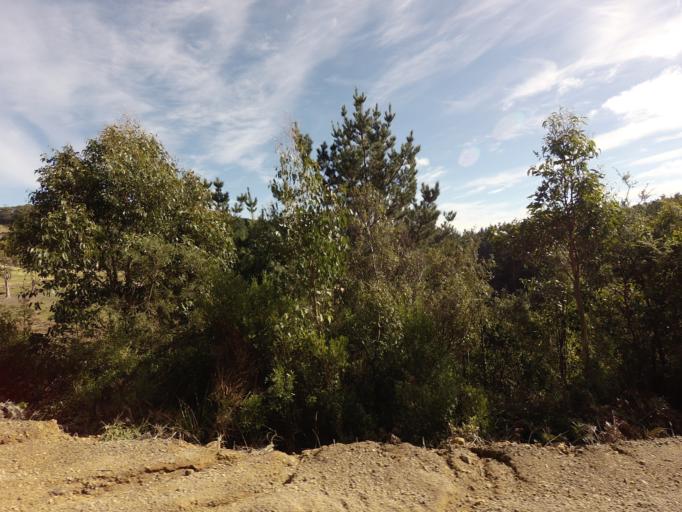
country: AU
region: Tasmania
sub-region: Clarence
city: Sandford
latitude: -43.1807
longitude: 147.7708
